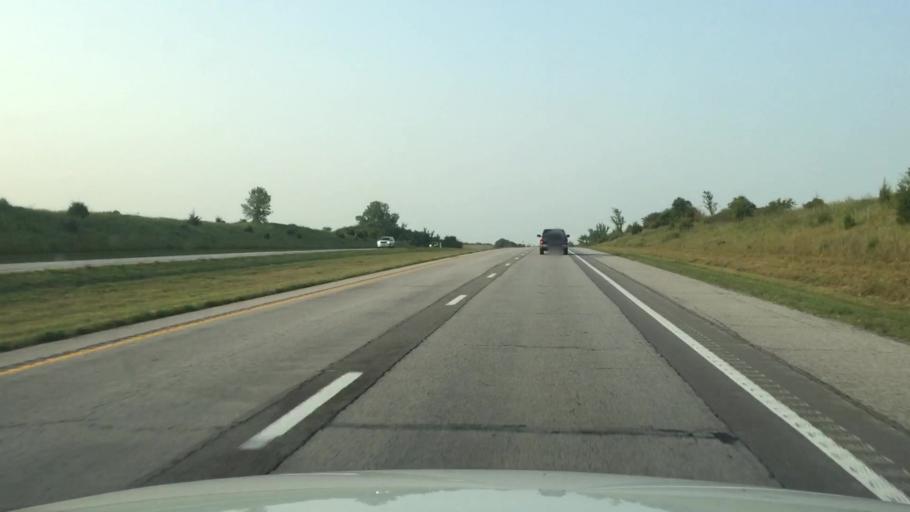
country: US
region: Missouri
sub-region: Harrison County
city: Bethany
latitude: 40.4201
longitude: -93.9899
